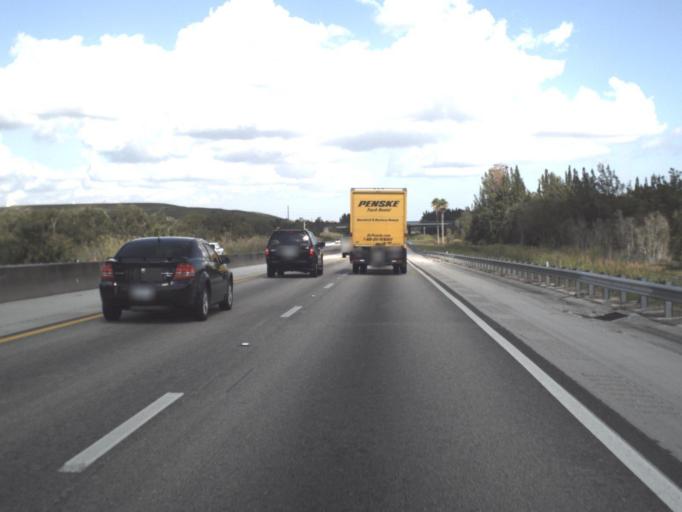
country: US
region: Florida
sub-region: Palm Beach County
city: Schall Circle
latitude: 26.7529
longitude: -80.1342
